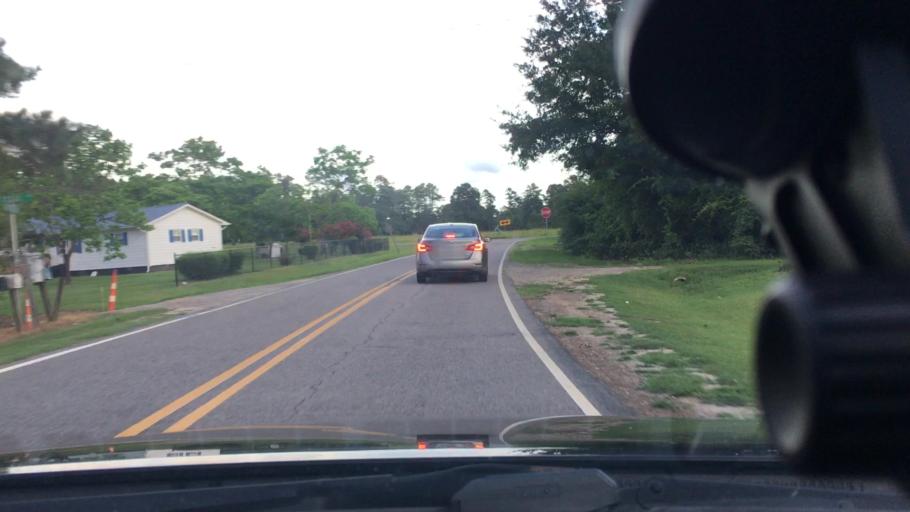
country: US
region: North Carolina
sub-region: Moore County
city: Carthage
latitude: 35.3610
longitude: -79.3267
